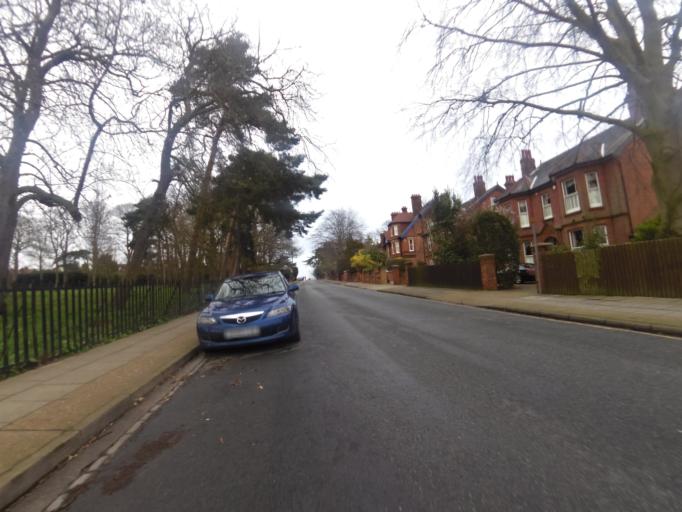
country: GB
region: England
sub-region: Suffolk
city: Ipswich
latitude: 52.0661
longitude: 1.1597
